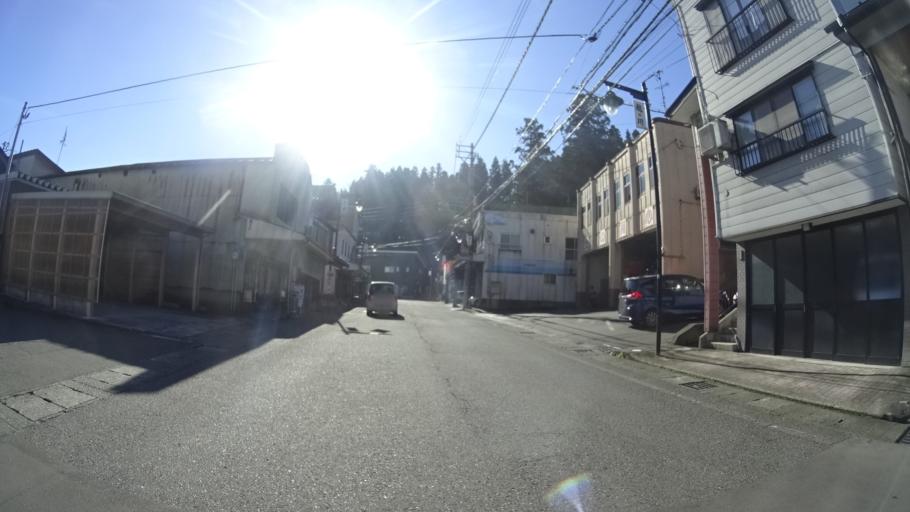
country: JP
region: Niigata
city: Tochio-honcho
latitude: 37.4764
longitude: 138.9924
